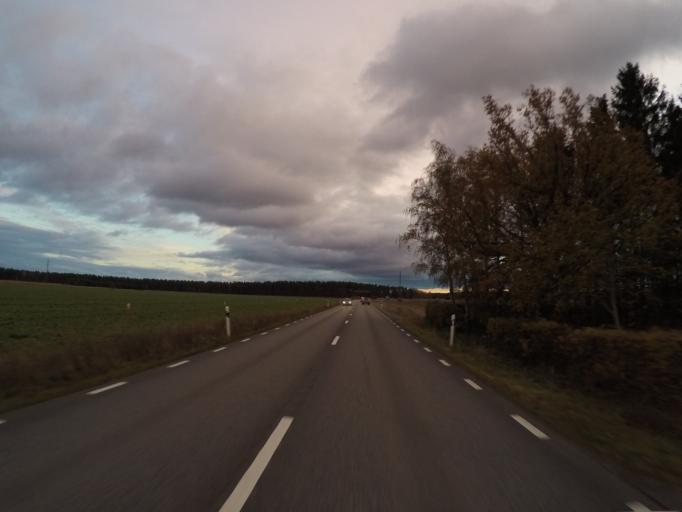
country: SE
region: Skane
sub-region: Kristianstads Kommun
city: Degeberga
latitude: 55.8897
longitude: 14.0861
